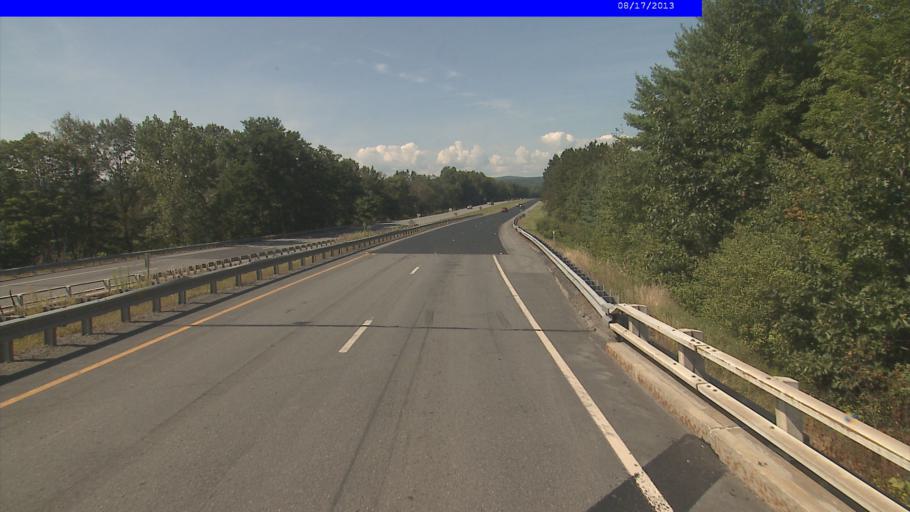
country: US
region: New Hampshire
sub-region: Cheshire County
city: Westmoreland
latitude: 42.9701
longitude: -72.4922
